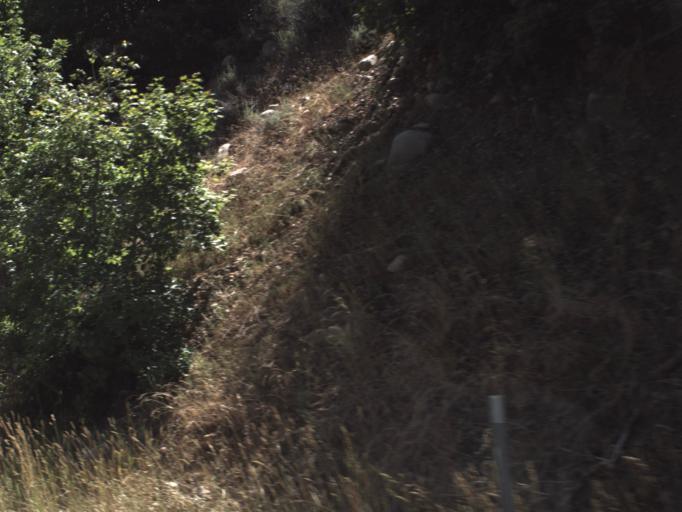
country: US
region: Utah
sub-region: Weber County
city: Wolf Creek
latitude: 41.3269
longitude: -111.6159
